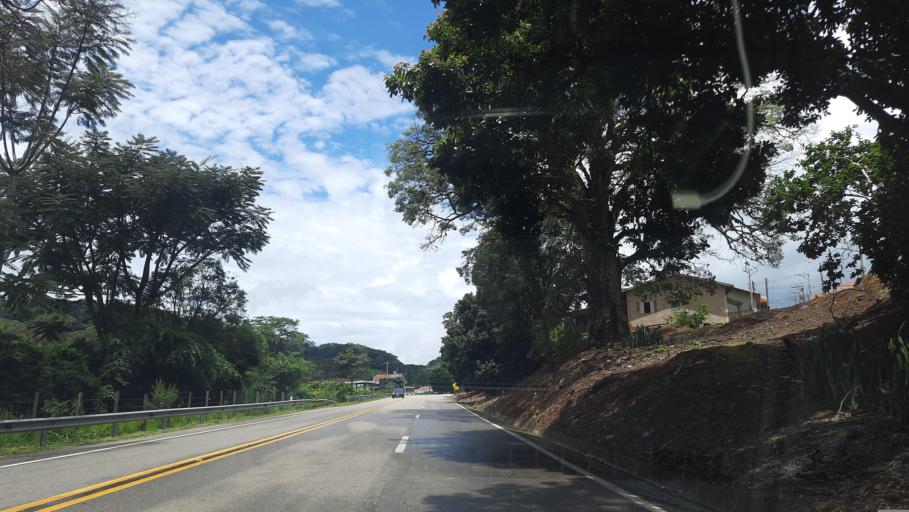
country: BR
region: Sao Paulo
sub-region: Sao Joao Da Boa Vista
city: Sao Joao da Boa Vista
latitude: -21.8355
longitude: -46.7465
